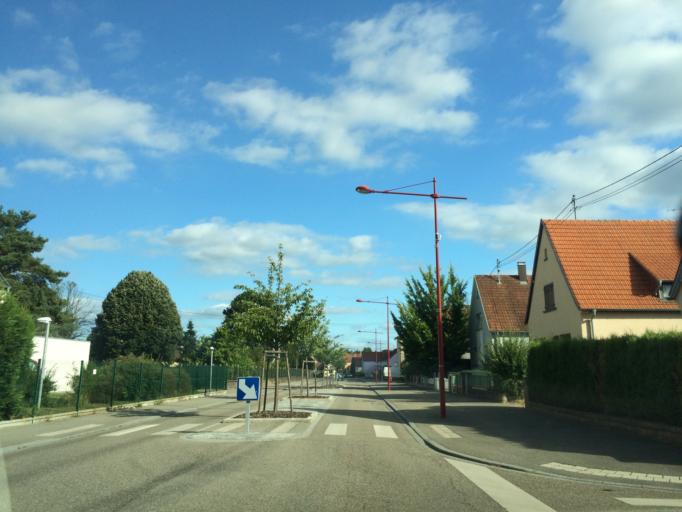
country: FR
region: Alsace
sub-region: Departement du Bas-Rhin
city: Soufflenheim
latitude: 48.8362
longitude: 7.9610
